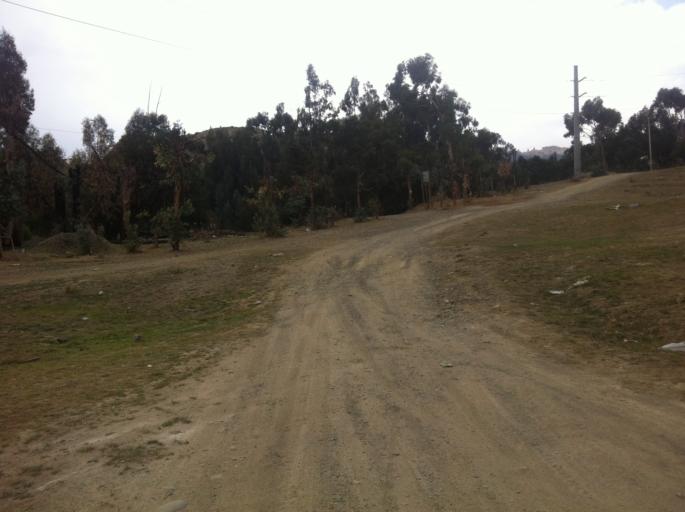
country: BO
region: La Paz
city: La Paz
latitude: -16.5375
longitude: -68.0652
